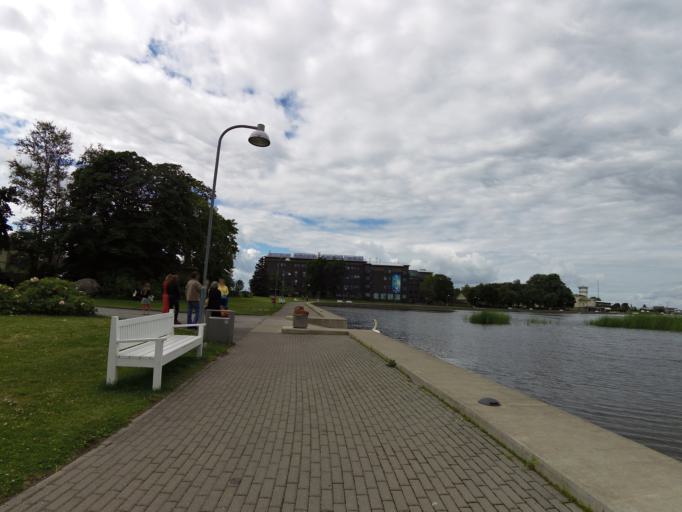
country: EE
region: Laeaene
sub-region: Haapsalu linn
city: Haapsalu
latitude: 58.9520
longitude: 23.5354
